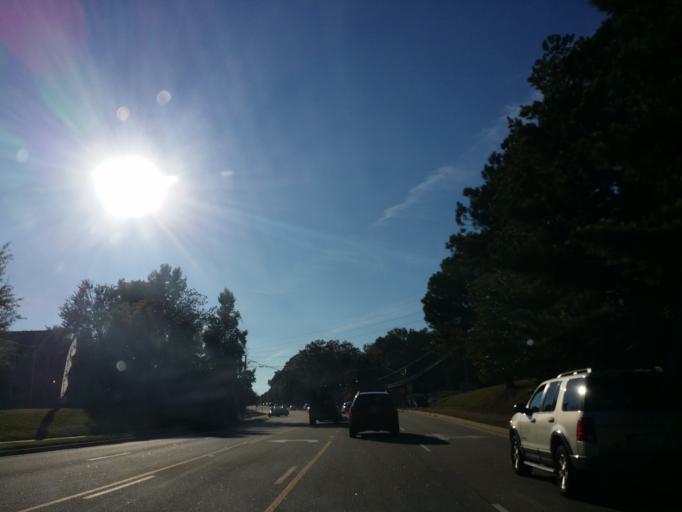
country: US
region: North Carolina
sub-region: Wake County
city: West Raleigh
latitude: 35.7686
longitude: -78.6930
